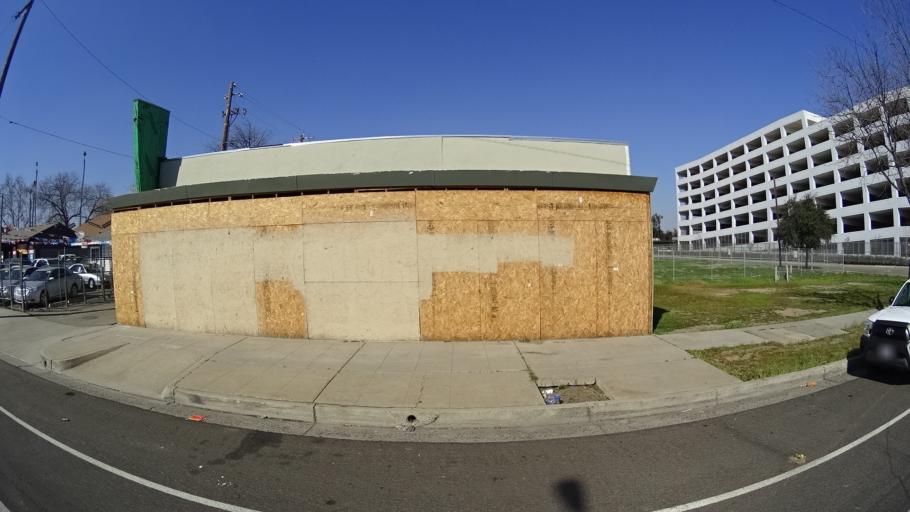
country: US
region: California
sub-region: Fresno County
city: Fresno
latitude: 36.7435
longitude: -119.7877
